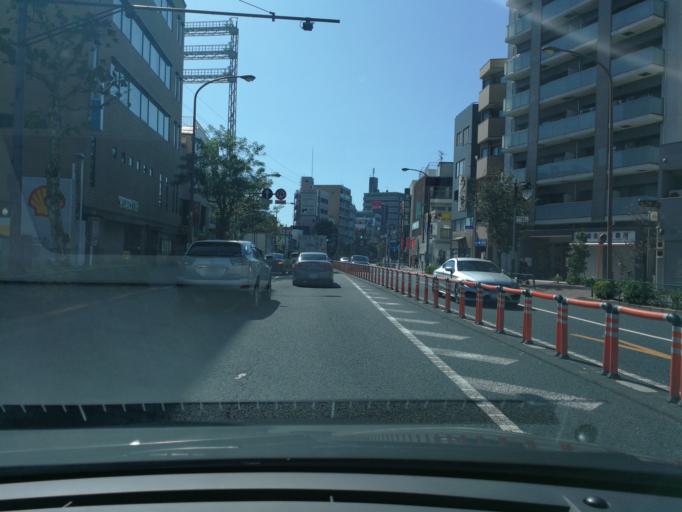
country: JP
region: Kanagawa
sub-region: Kawasaki-shi
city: Kawasaki
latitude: 35.5927
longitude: 139.6809
